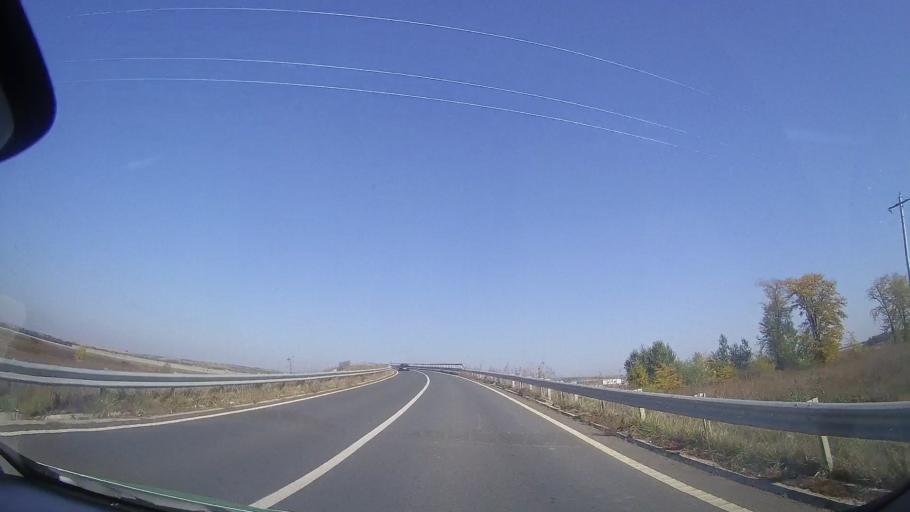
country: RO
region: Timis
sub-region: Comuna Balint
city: Balint
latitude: 45.7964
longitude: 21.8609
